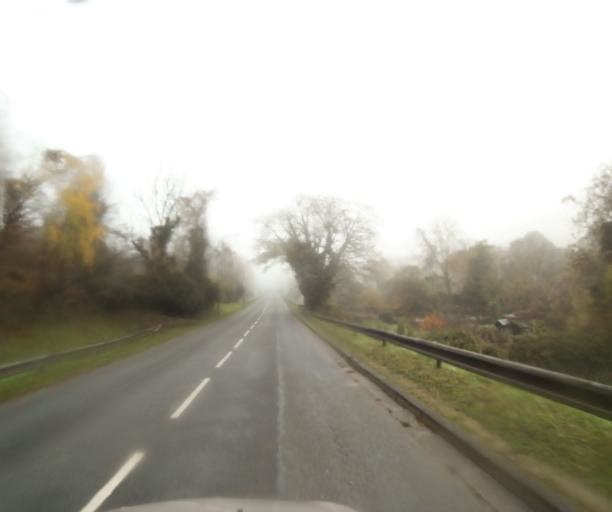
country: FR
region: Ile-de-France
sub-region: Departement de Seine-Saint-Denis
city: Vaujours
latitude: 48.9290
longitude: 2.5701
